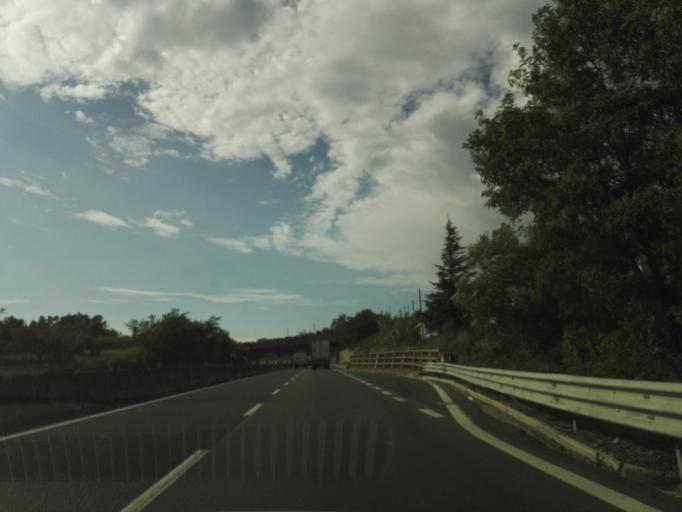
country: IT
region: Calabria
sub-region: Provincia di Catanzaro
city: Marcellinara
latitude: 38.9148
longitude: 16.4922
